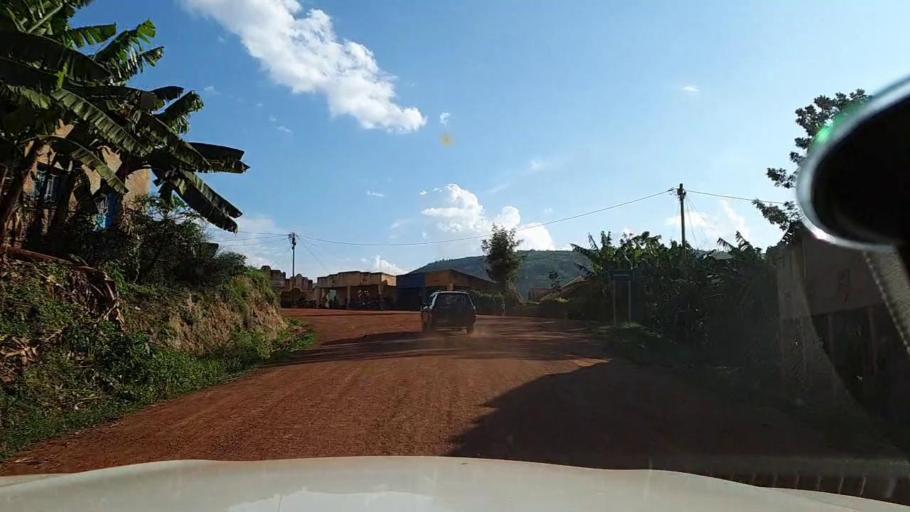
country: RW
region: Kigali
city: Kigali
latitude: -1.8642
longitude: 29.9233
